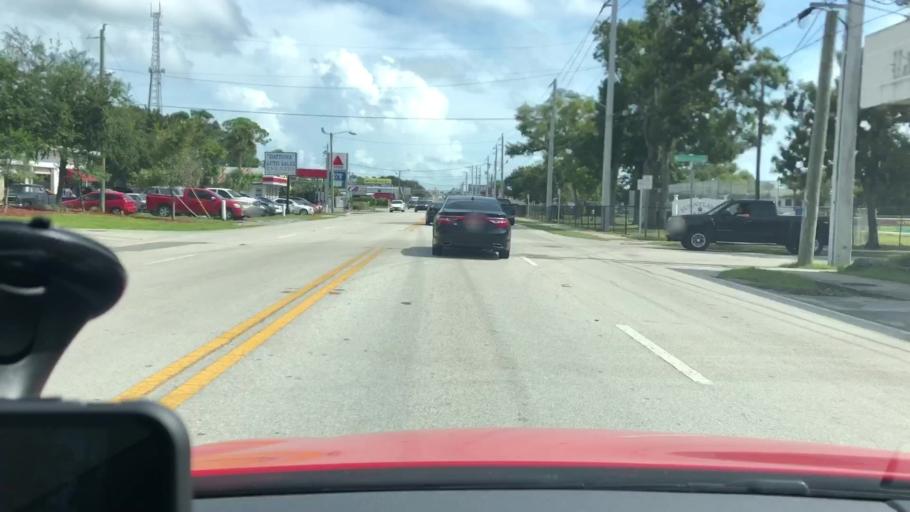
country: US
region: Florida
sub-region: Volusia County
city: Daytona Beach
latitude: 29.2241
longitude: -81.0370
